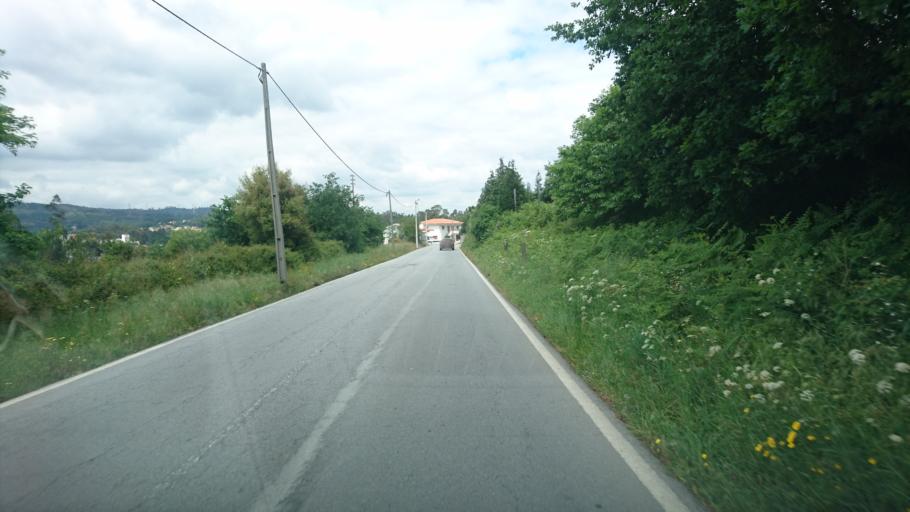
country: PT
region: Porto
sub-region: Paredes
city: Baltar
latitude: 41.1642
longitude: -8.3551
